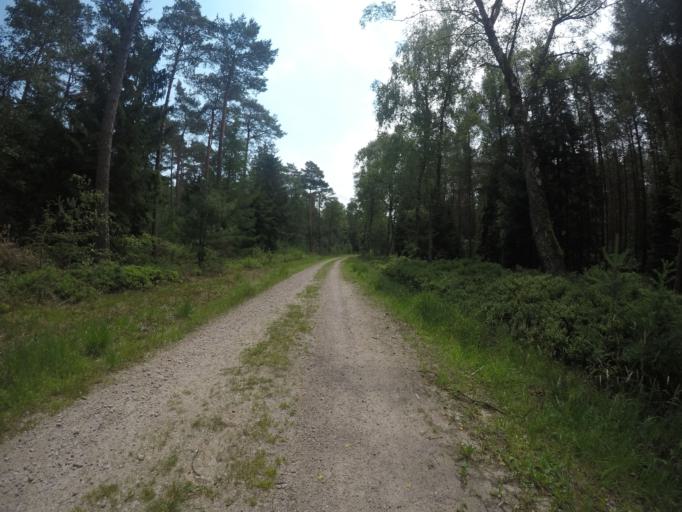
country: DE
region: Lower Saxony
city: Jesteburg
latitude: 53.2597
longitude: 9.9330
